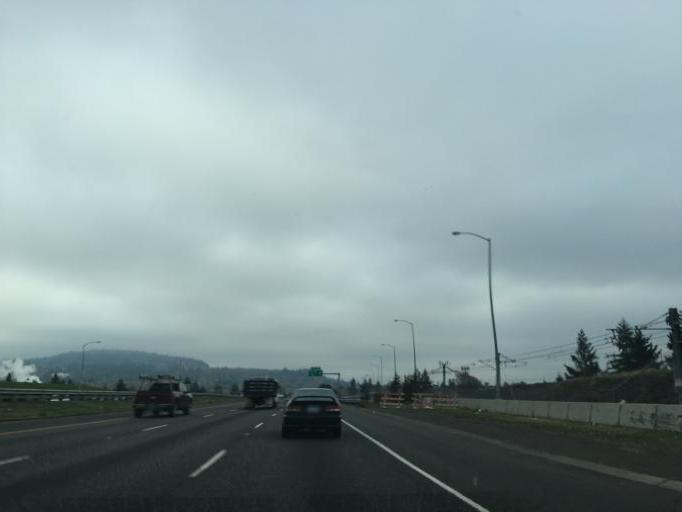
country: US
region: Oregon
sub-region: Multnomah County
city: Lents
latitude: 45.4846
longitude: -122.5664
